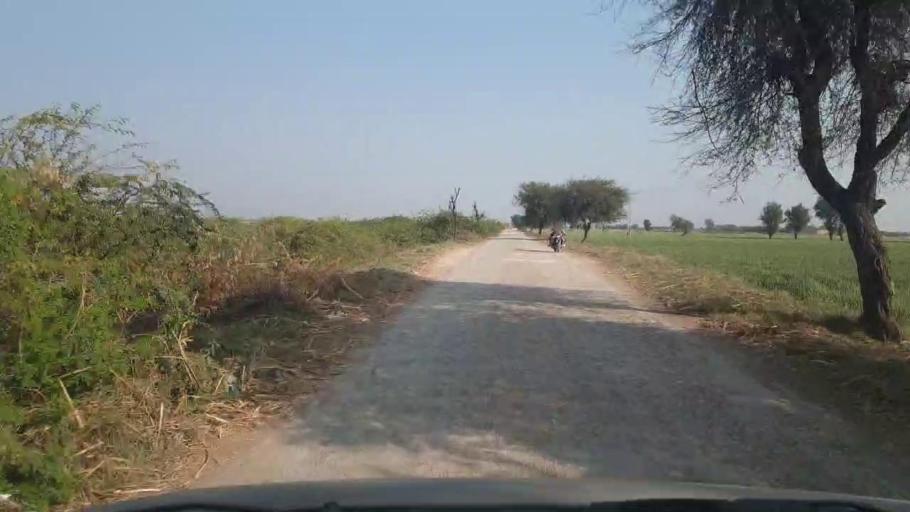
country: PK
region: Sindh
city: Digri
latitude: 25.2416
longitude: 69.1866
